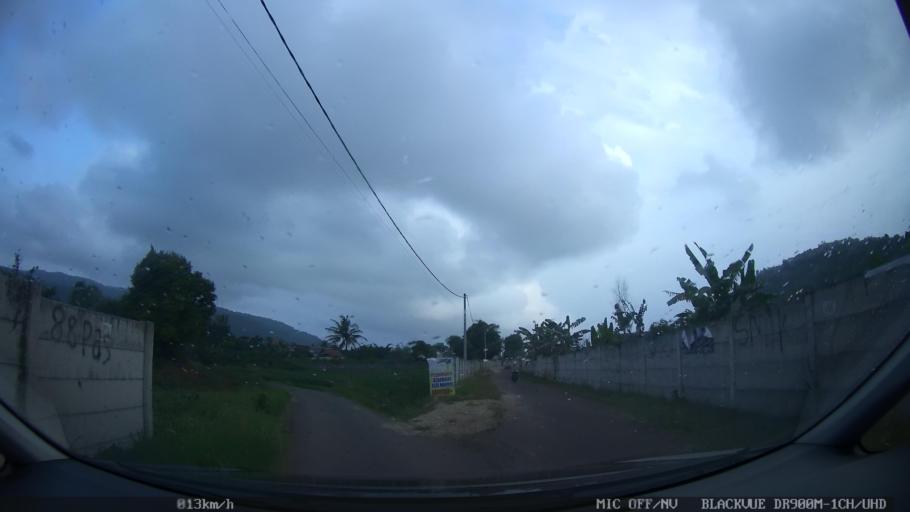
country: ID
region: Lampung
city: Bandarlampung
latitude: -5.4195
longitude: 105.2900
